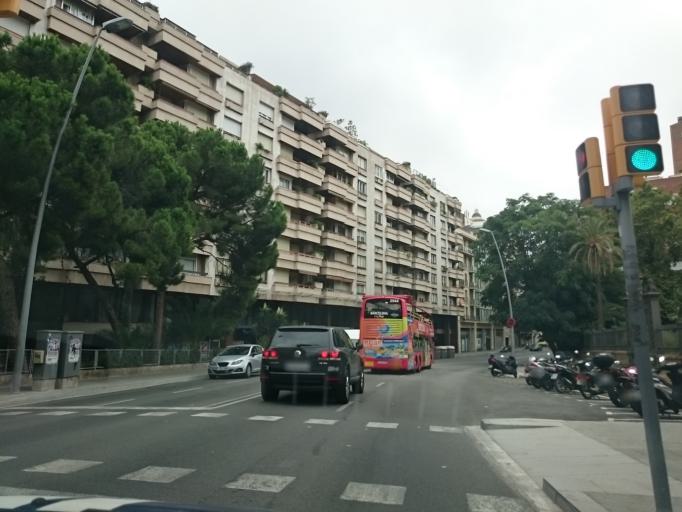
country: ES
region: Catalonia
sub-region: Provincia de Barcelona
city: Sarria-Sant Gervasi
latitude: 41.4081
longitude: 2.1343
